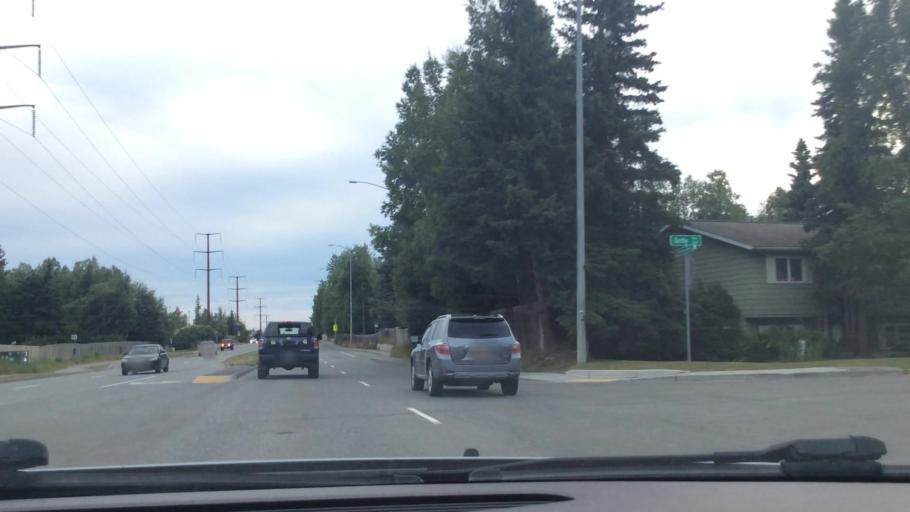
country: US
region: Alaska
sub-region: Anchorage Municipality
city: Anchorage
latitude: 61.1953
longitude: -149.7673
